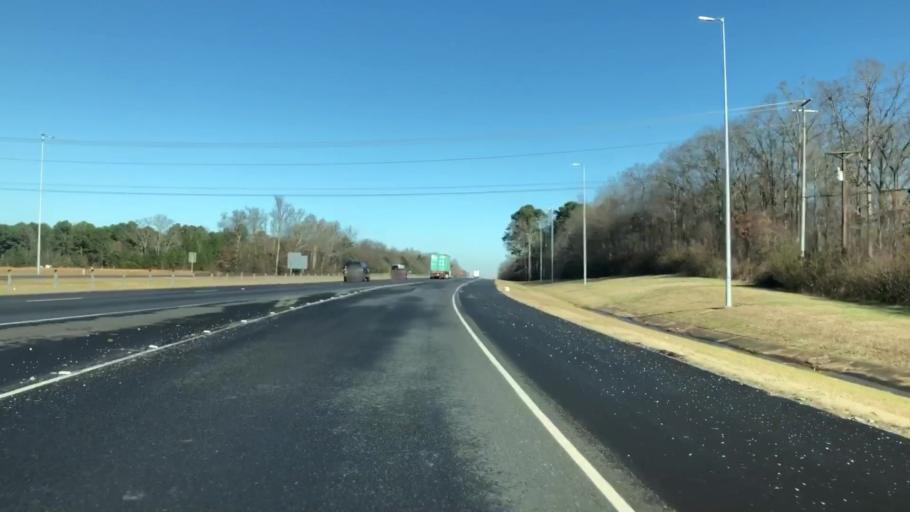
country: US
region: Alabama
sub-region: Limestone County
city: Athens
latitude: 34.7853
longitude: -86.9394
